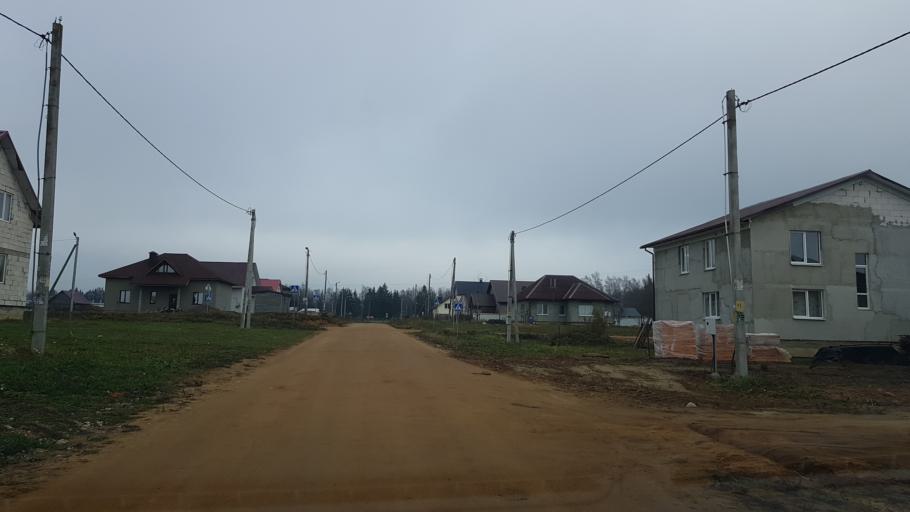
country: BY
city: Fanipol
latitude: 53.7290
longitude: 27.3286
